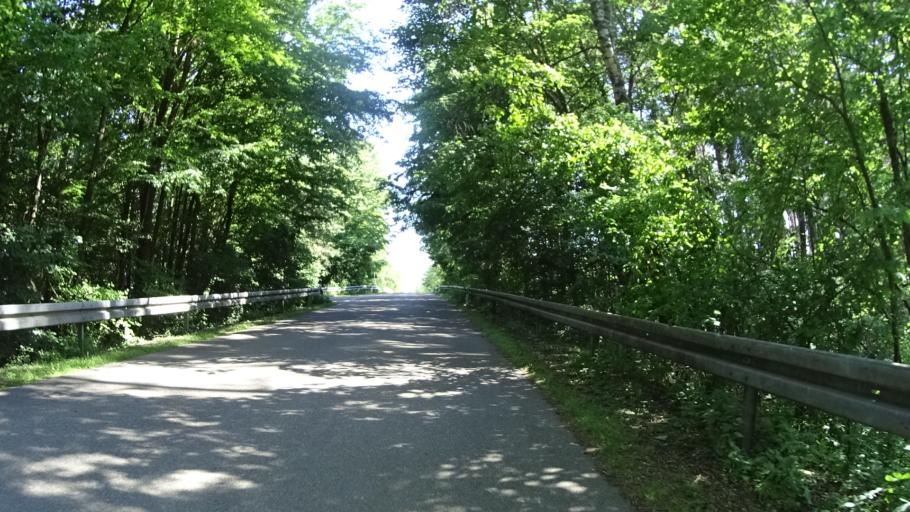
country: DE
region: Bavaria
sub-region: Regierungsbezirk Mittelfranken
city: Dombuhl
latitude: 49.2298
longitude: 10.2965
